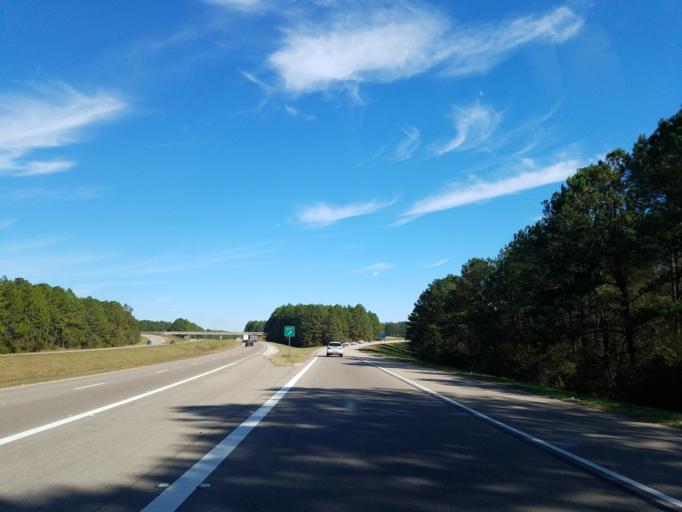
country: US
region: Mississippi
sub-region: Forrest County
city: Hattiesburg
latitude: 31.2428
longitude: -89.2820
